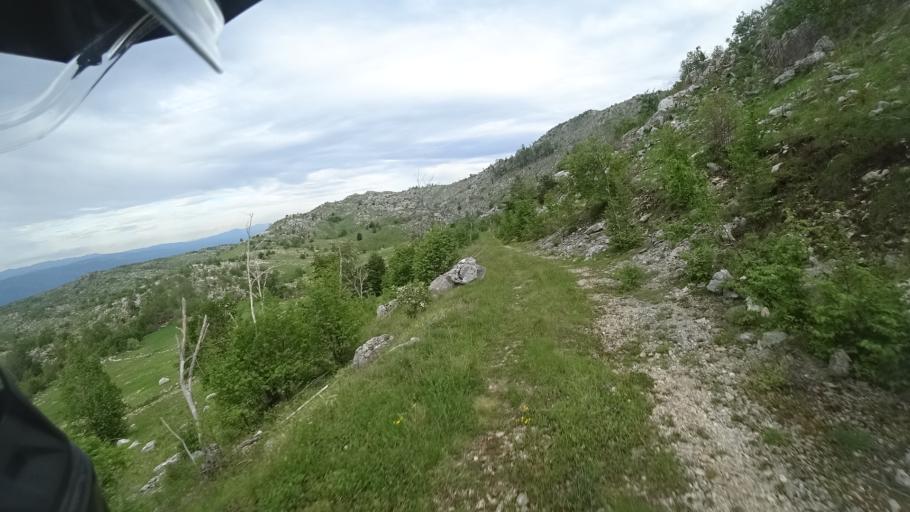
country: HR
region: Sibensko-Kniniska
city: Drnis
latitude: 43.8575
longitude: 16.3854
